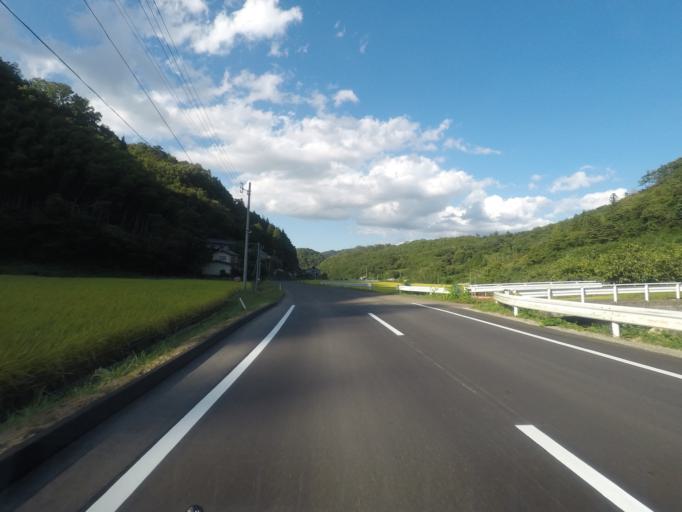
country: JP
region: Fukushima
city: Hobaramachi
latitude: 37.7509
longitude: 140.5588
